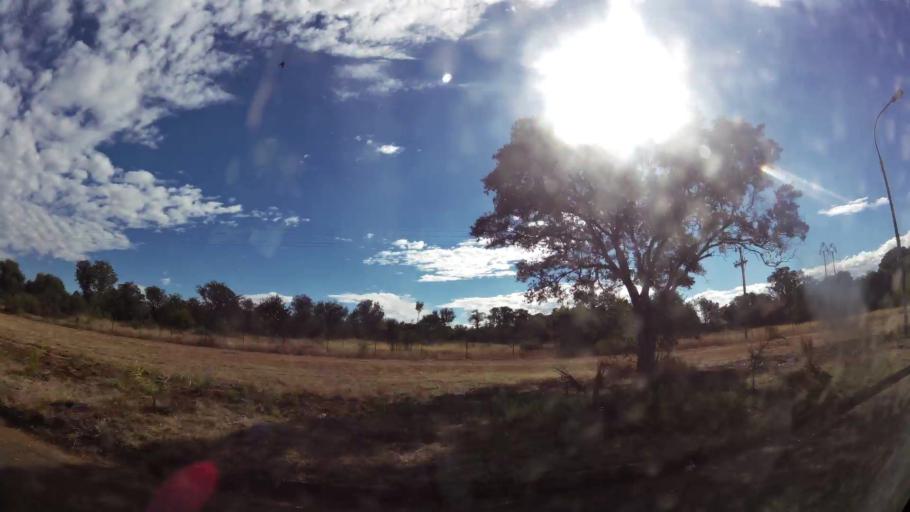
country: ZA
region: Limpopo
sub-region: Waterberg District Municipality
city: Warmbaths
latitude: -24.8787
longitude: 28.2761
